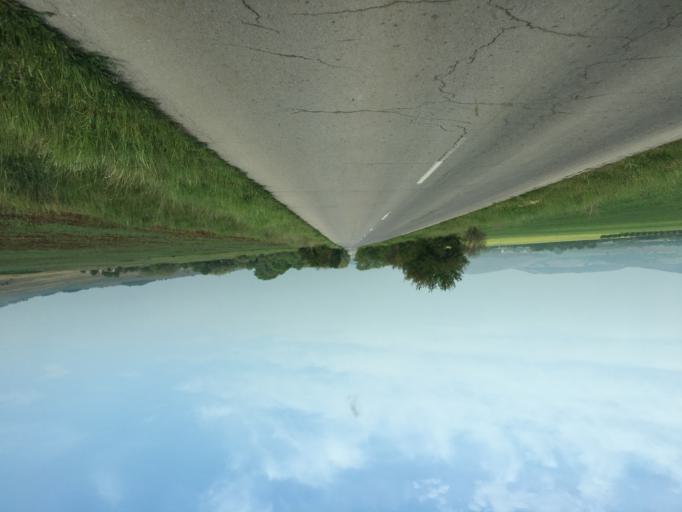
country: BG
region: Kyustendil
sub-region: Obshtina Bobovdol
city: Bobovdol
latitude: 42.4604
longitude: 23.0931
